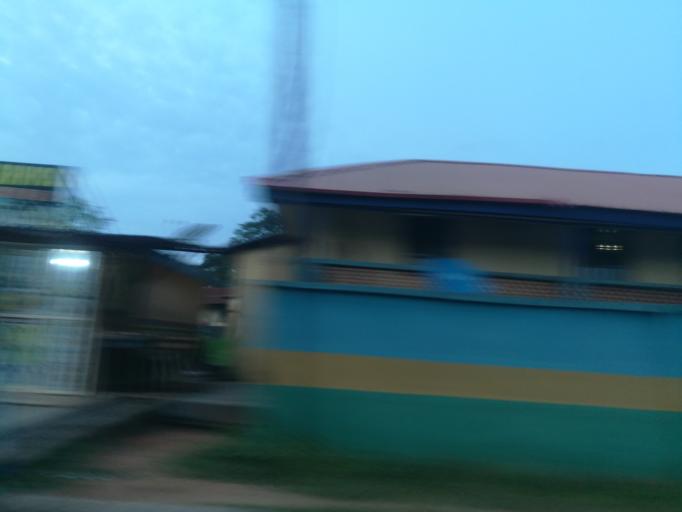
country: NG
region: Oyo
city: Ibadan
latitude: 7.3962
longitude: 3.9074
